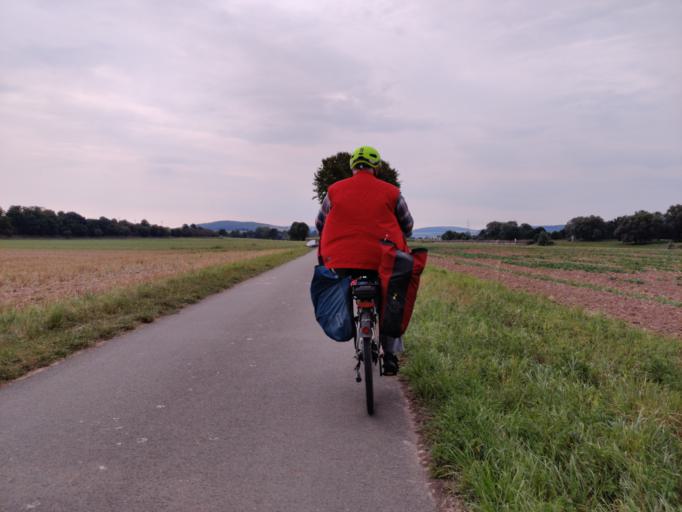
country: DE
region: Lower Saxony
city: Hehlen
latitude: 52.0407
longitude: 9.4151
